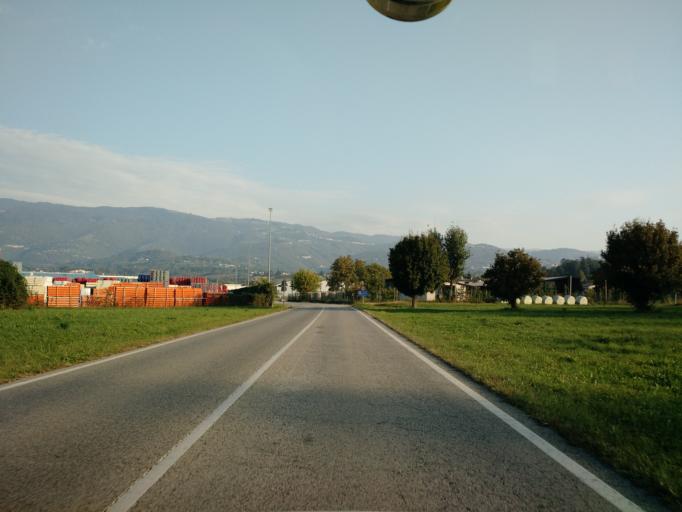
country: IT
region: Veneto
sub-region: Provincia di Vicenza
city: Zugliano
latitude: 45.7231
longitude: 11.5420
